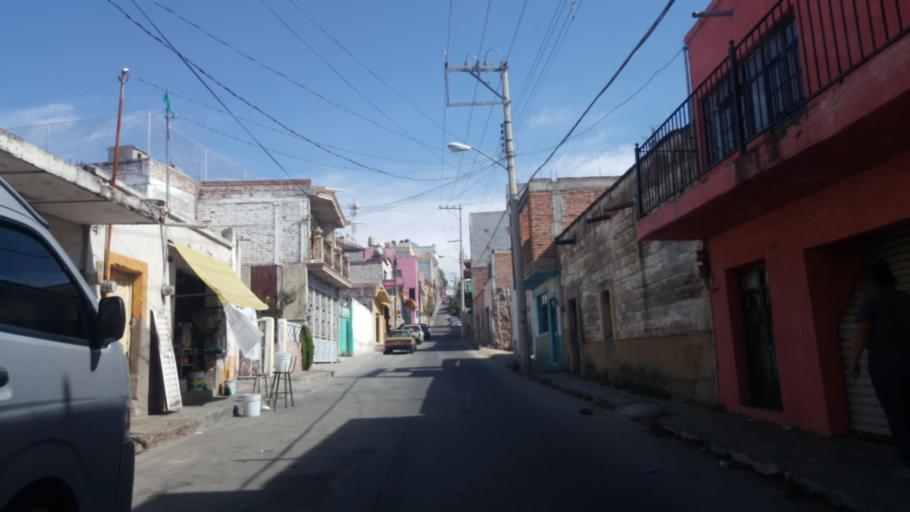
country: MX
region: Jalisco
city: San Juan de los Lagos
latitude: 21.2495
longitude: -102.3357
